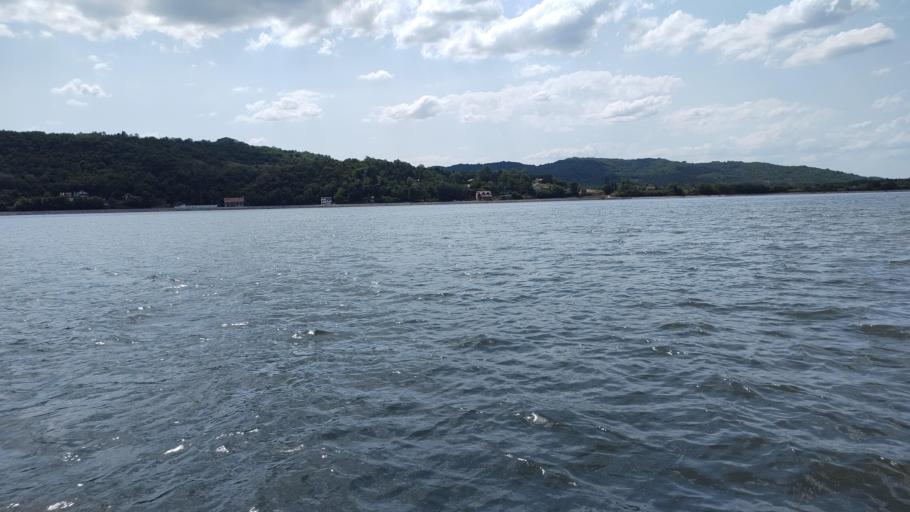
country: RS
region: Central Serbia
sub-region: Branicevski Okrug
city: Golubac
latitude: 44.6648
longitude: 21.6237
